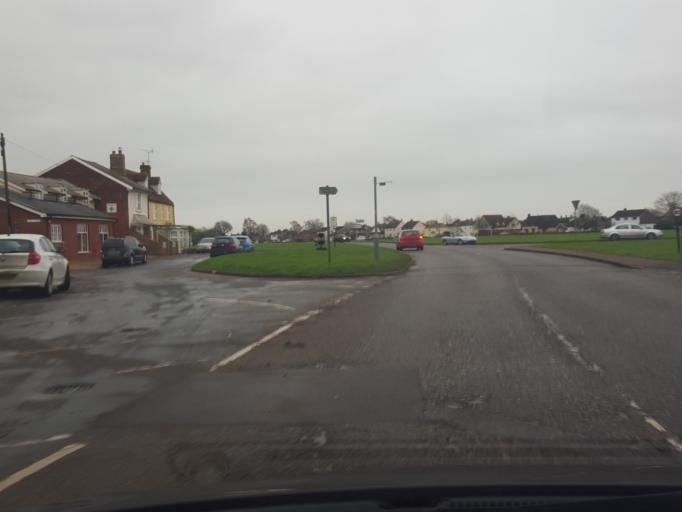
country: GB
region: England
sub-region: Essex
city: Great Bentley
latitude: 51.8549
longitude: 1.0618
